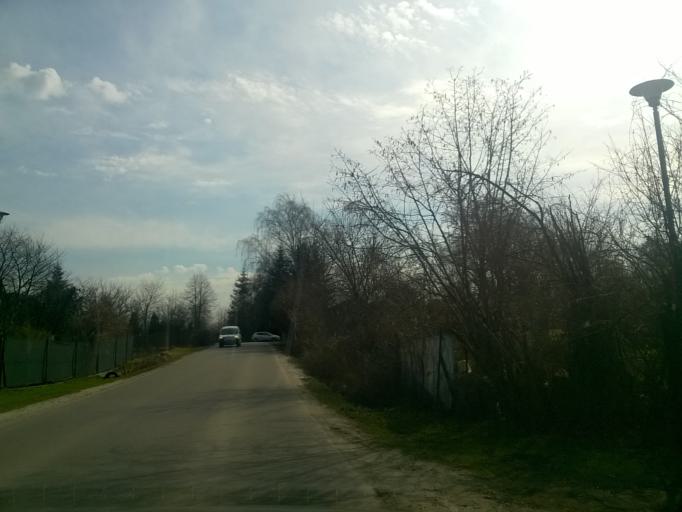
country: PL
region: Lesser Poland Voivodeship
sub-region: Powiat krakowski
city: Rzaska
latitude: 50.0892
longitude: 19.8626
